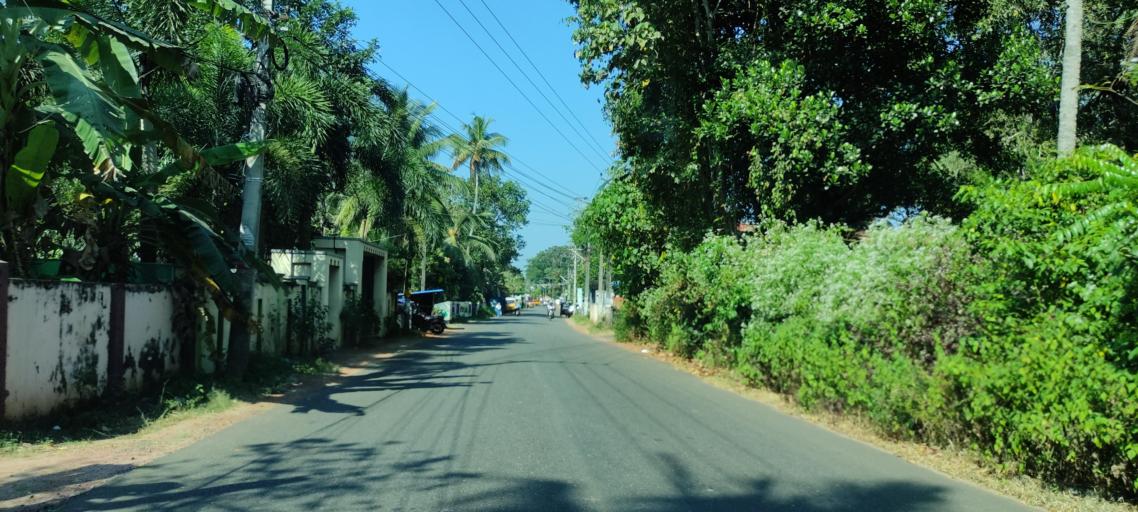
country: IN
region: Kerala
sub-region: Kollam
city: Panmana
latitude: 9.0410
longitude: 76.5933
